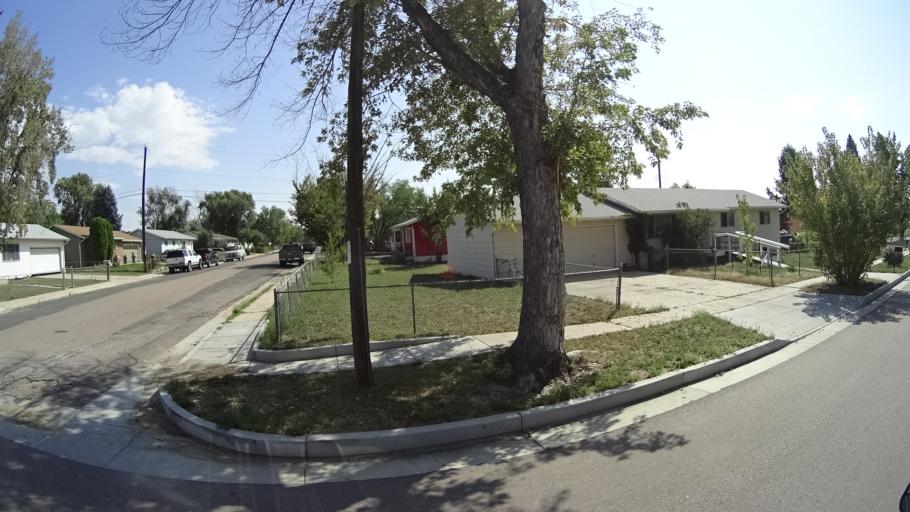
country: US
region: Colorado
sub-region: El Paso County
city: Colorado Springs
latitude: 38.8181
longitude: -104.7898
